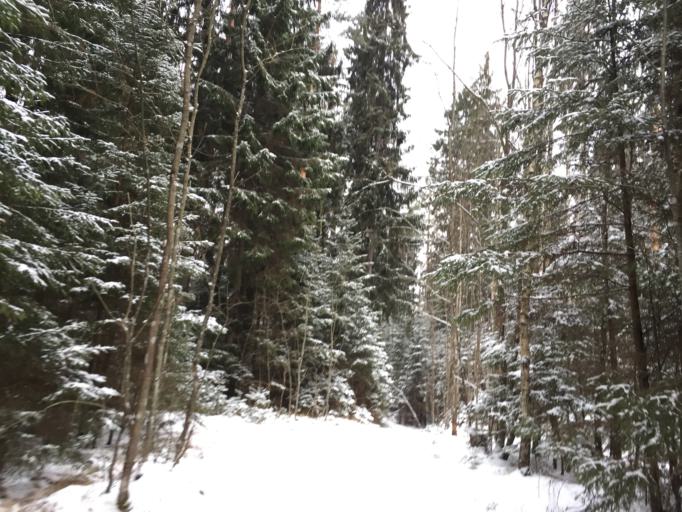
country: LV
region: Ligatne
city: Ligatne
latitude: 57.2405
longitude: 25.0511
